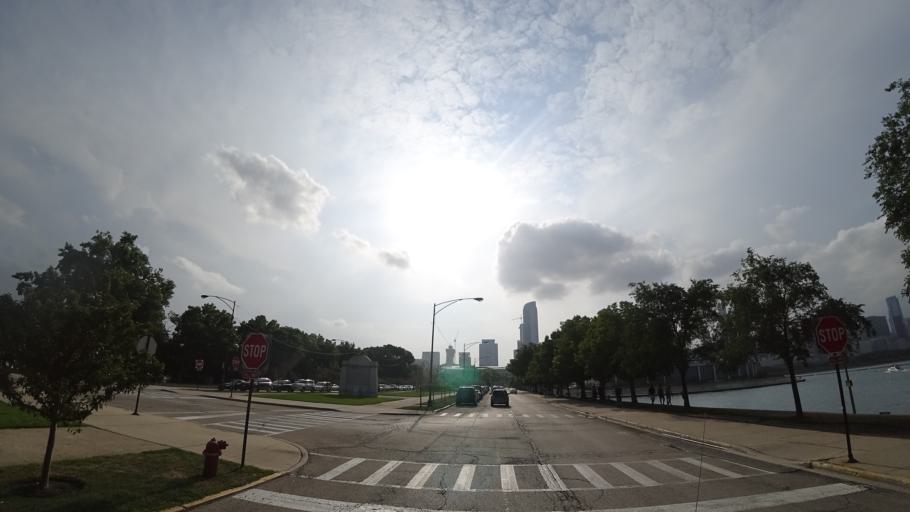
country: US
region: Illinois
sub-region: Cook County
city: Chicago
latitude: 41.8665
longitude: -87.6098
